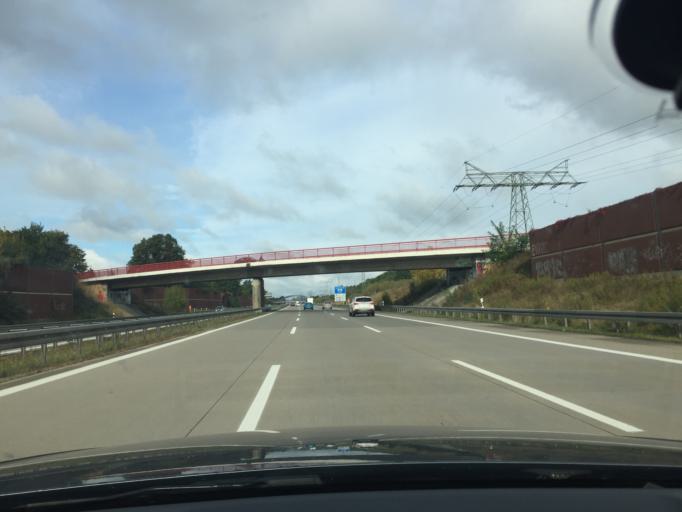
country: DE
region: Brandenburg
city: Neuenhagen
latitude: 52.5151
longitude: 13.7280
